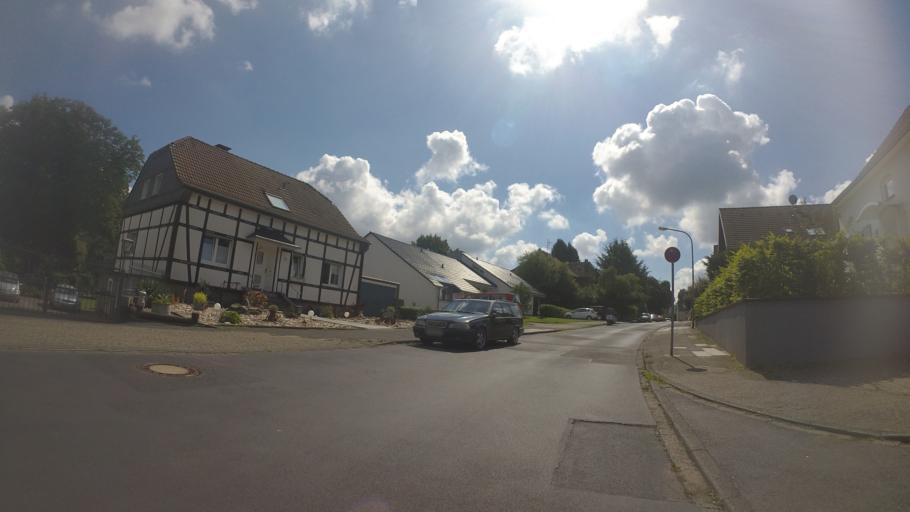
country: DE
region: North Rhine-Westphalia
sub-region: Regierungsbezirk Dusseldorf
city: Remscheid
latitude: 51.2105
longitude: 7.2436
